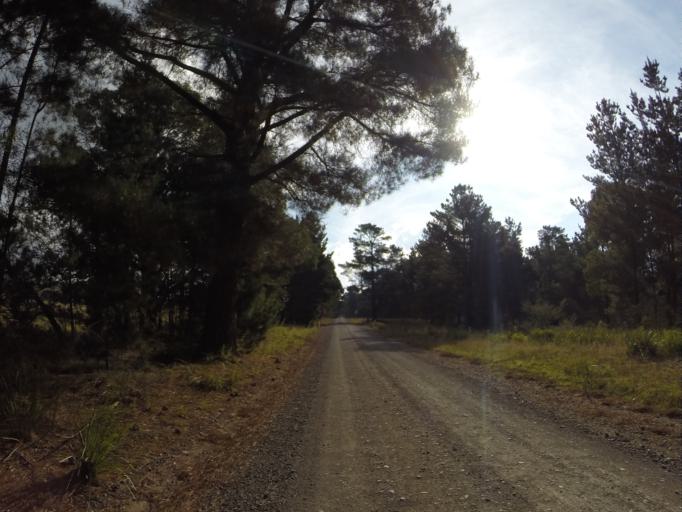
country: AU
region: New South Wales
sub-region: Wingecarribee
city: Bundanoon
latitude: -34.5336
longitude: 150.2256
